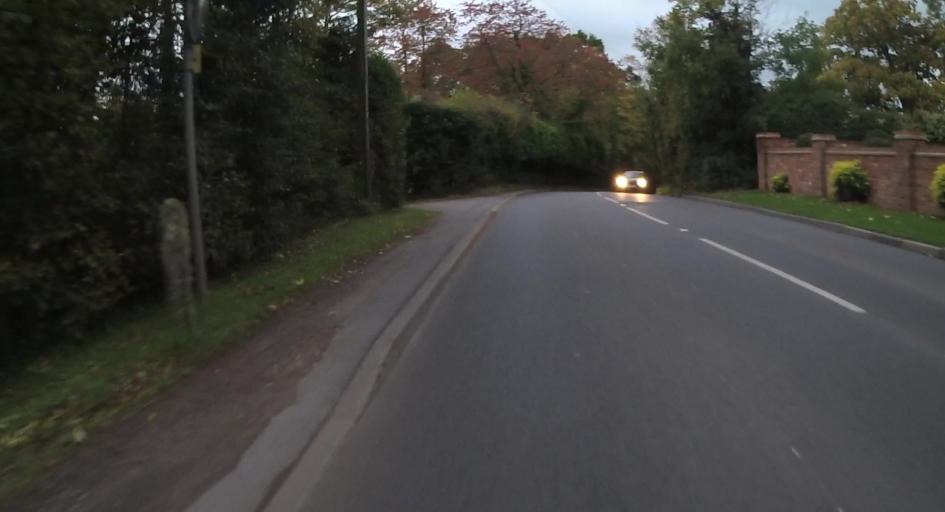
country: GB
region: England
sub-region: Wokingham
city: Finchampstead
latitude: 51.3645
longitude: -0.8555
